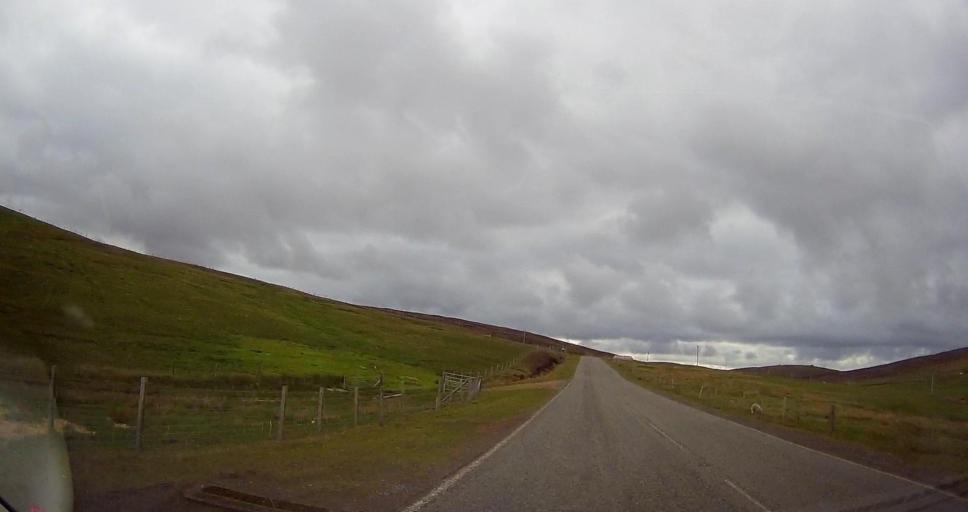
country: GB
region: Scotland
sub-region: Shetland Islands
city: Shetland
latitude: 60.6054
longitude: -1.1111
